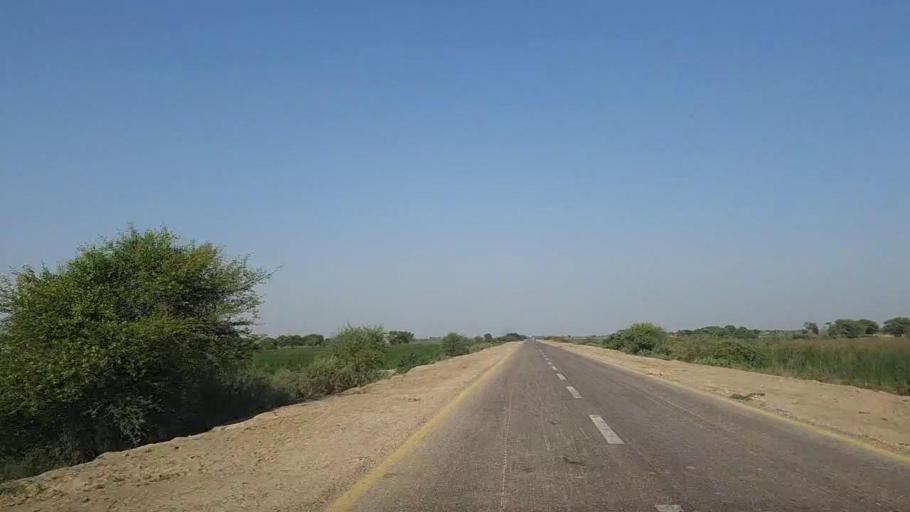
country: PK
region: Sindh
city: Jati
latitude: 24.3924
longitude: 68.2884
